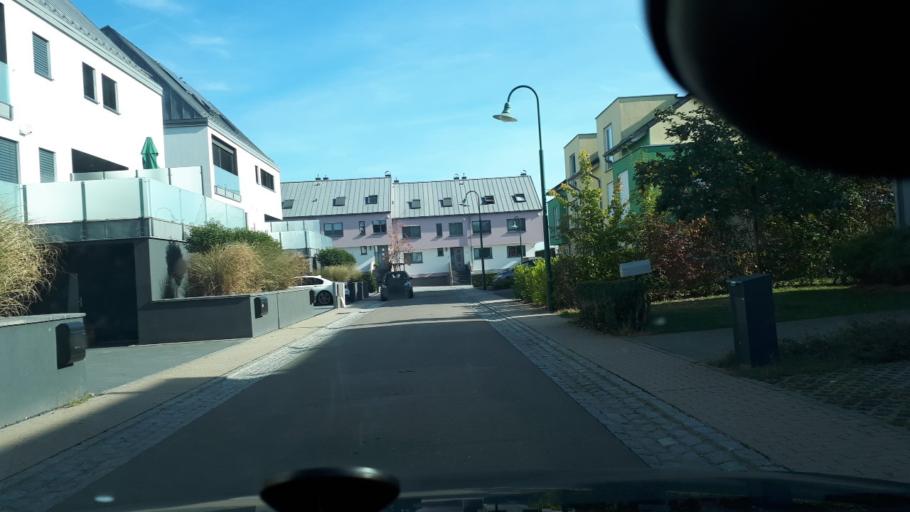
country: LU
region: Grevenmacher
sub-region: Canton de Grevenmacher
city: Flaxweiler
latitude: 49.6712
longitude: 6.3014
